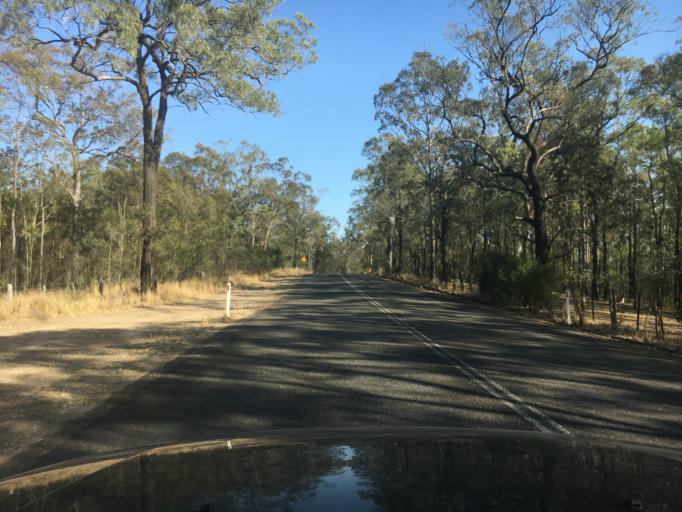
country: AU
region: New South Wales
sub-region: Cessnock
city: Branxton
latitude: -32.5644
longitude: 151.3221
